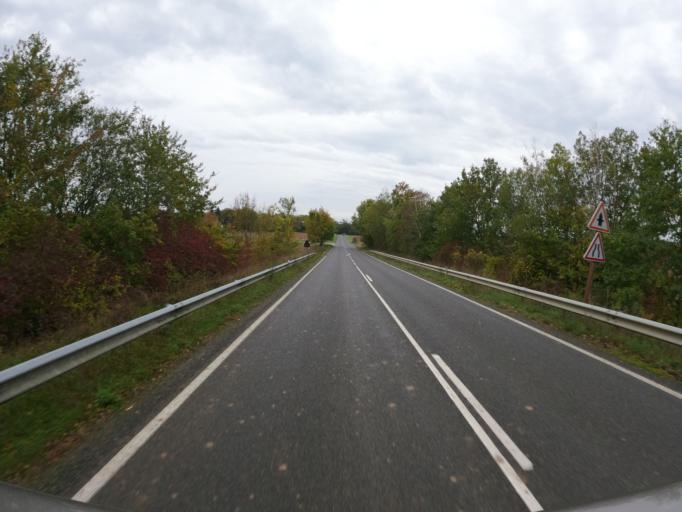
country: FR
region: Ile-de-France
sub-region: Departement de Seine-et-Marne
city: Serris
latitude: 48.8202
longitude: 2.7800
